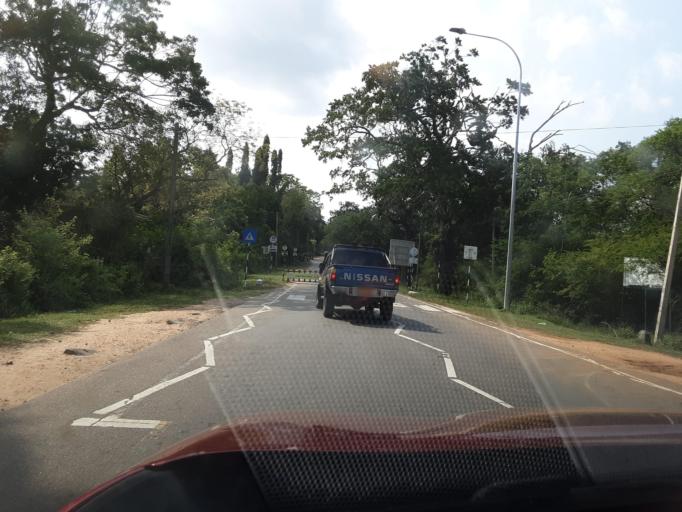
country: LK
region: Uva
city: Haputale
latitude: 6.3614
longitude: 81.1808
